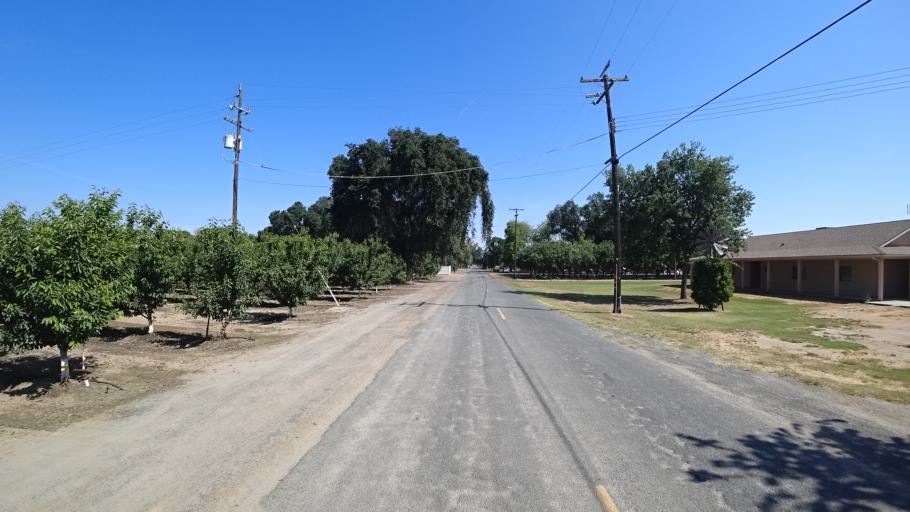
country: US
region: California
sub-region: Kings County
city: Lemoore
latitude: 36.3522
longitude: -119.8250
